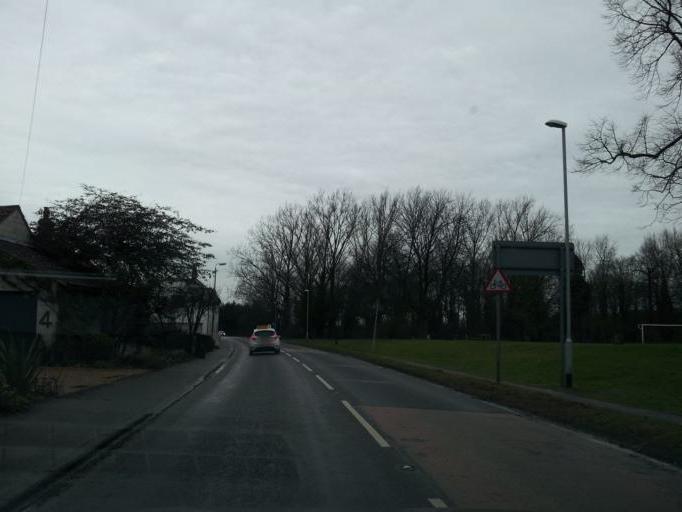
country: GB
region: England
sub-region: Cambridgeshire
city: Bottisham
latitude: 52.2399
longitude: 0.2771
